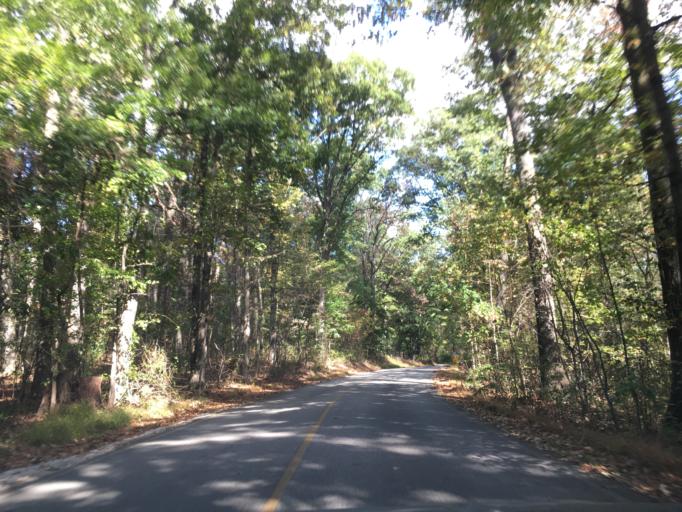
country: US
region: Pennsylvania
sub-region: York County
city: Yorklyn
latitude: 40.0090
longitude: -76.6617
